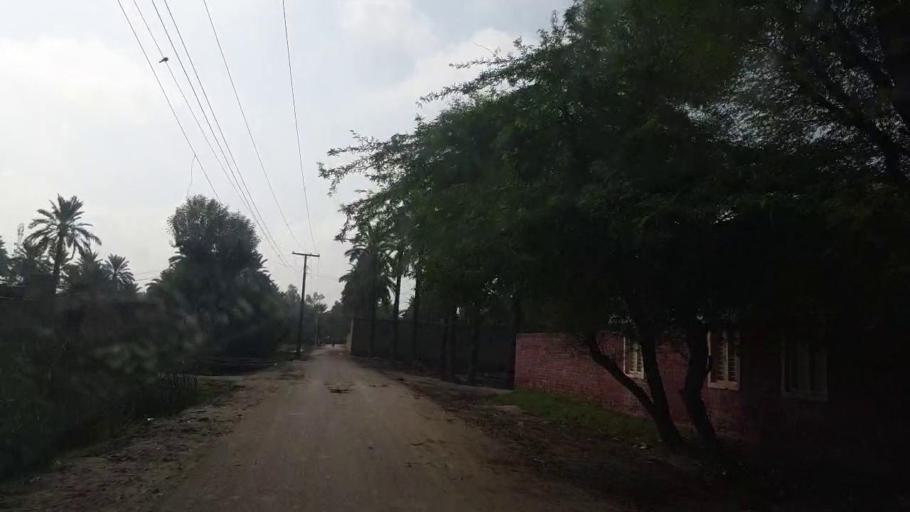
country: PK
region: Sindh
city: Khairpur
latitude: 27.5878
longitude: 68.7728
